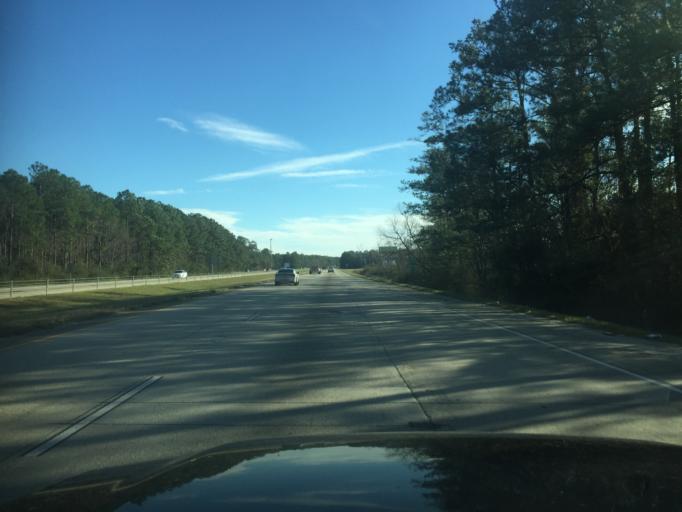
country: US
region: Louisiana
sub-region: Saint Tammany Parish
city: Pearl River
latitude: 30.3497
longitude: -89.7401
